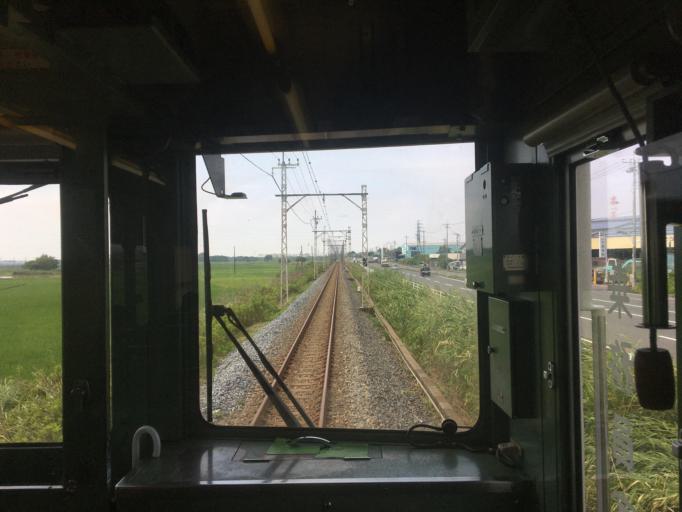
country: JP
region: Tochigi
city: Sano
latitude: 36.2846
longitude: 139.5616
